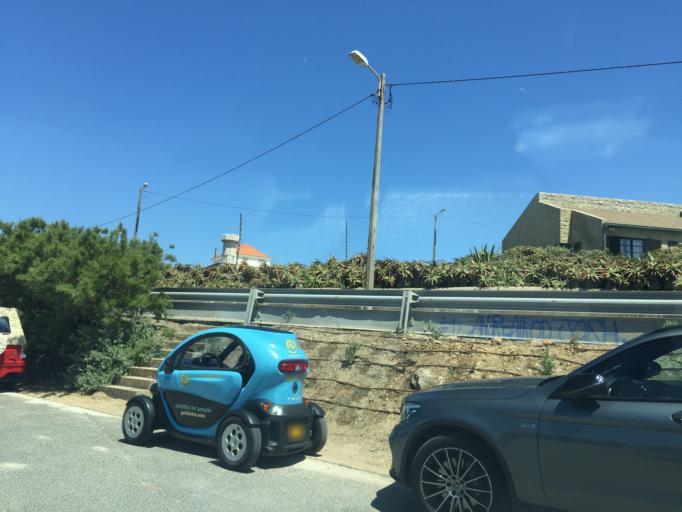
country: PT
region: Lisbon
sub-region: Sintra
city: Colares
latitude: 38.8390
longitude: -9.4636
